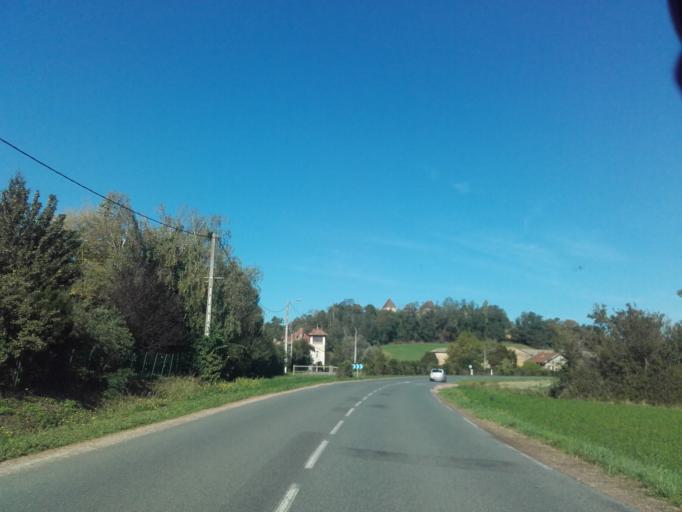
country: FR
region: Bourgogne
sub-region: Departement de Saone-et-Loire
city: Charnay-les-Macon
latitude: 46.2929
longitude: 4.7701
